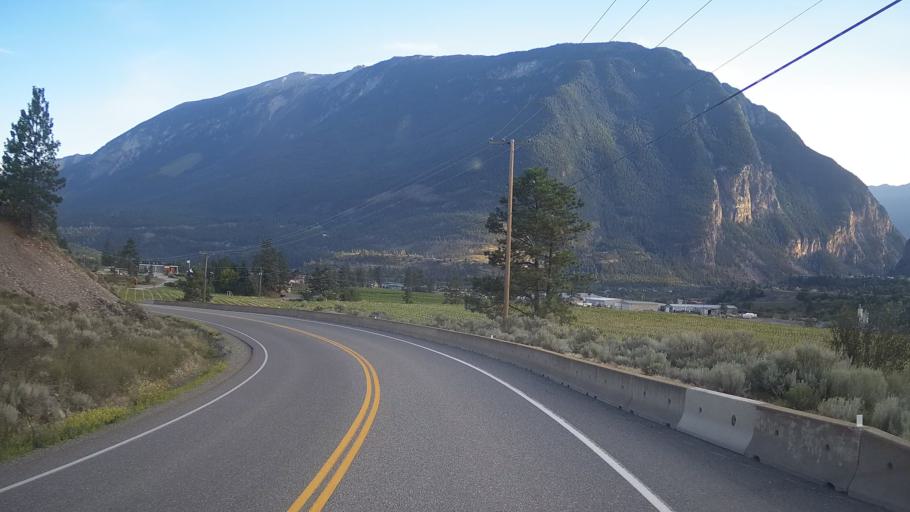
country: CA
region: British Columbia
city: Lillooet
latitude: 50.6924
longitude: -121.9213
